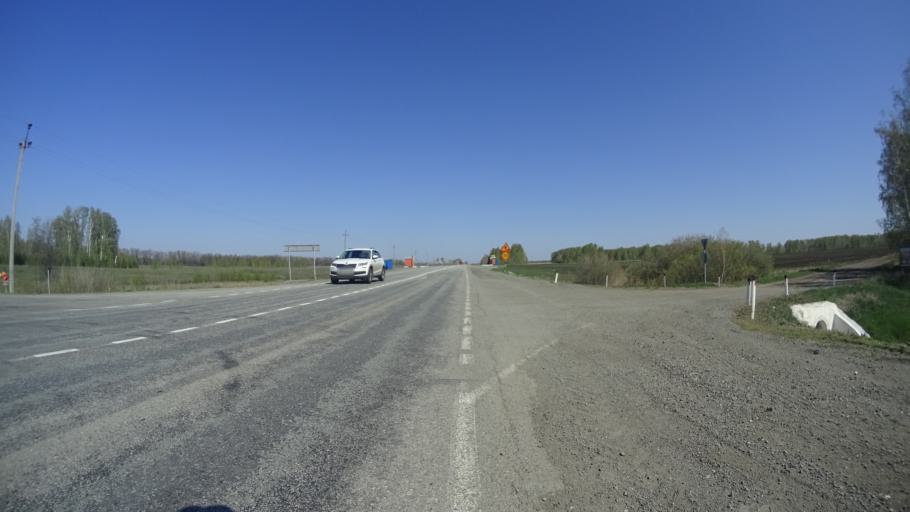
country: RU
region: Chelyabinsk
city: Troitsk
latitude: 54.1870
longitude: 61.4340
